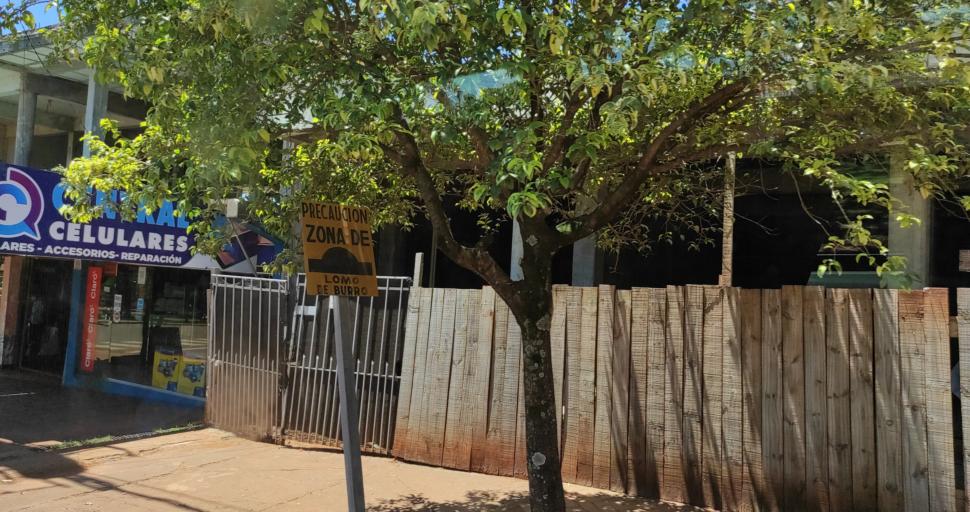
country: AR
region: Misiones
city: Dos de Mayo
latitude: -26.9935
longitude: -54.4802
